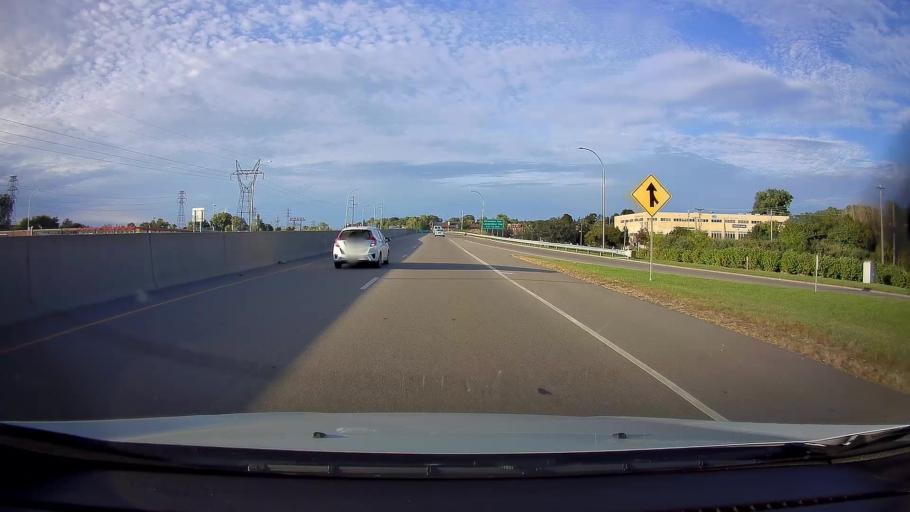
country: US
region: Minnesota
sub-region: Ramsey County
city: Lauderdale
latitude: 44.9848
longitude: -93.2033
